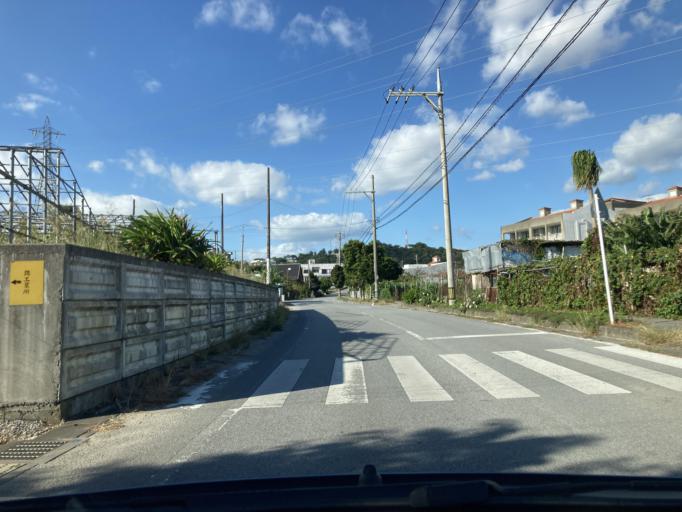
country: JP
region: Okinawa
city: Ginowan
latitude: 26.2198
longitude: 127.7557
